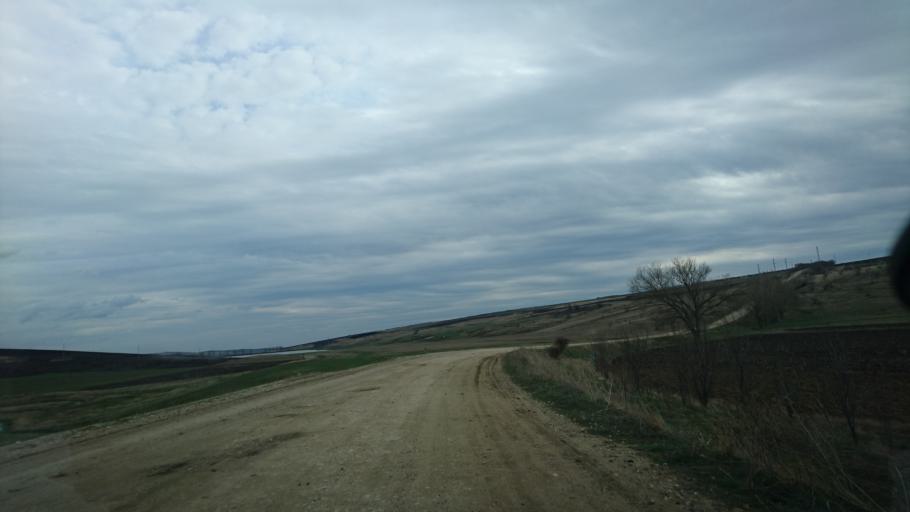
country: MD
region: Cantemir
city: Visniovca
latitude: 46.3137
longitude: 28.4066
